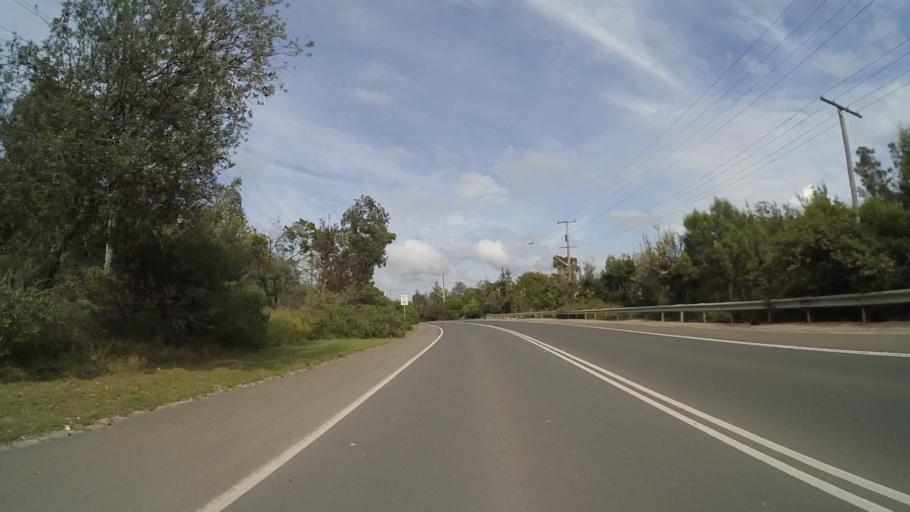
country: AU
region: New South Wales
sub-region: Rockdale
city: Dolls Point
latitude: -34.0238
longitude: 151.1669
